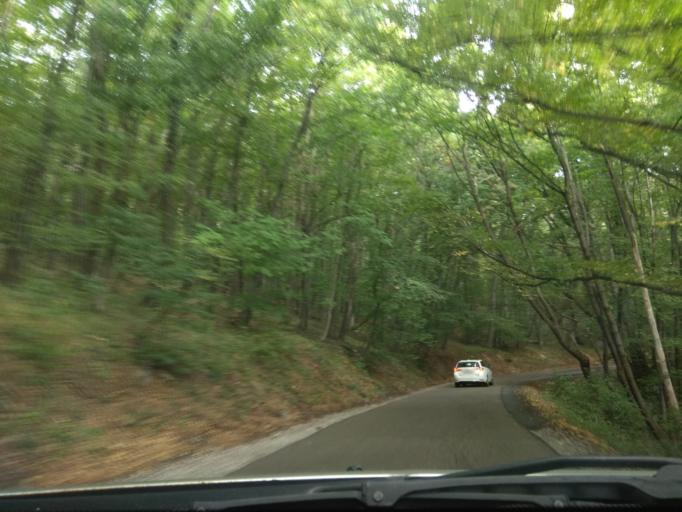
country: HU
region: Borsod-Abauj-Zemplen
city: Sajobabony
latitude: 48.0677
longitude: 20.6700
